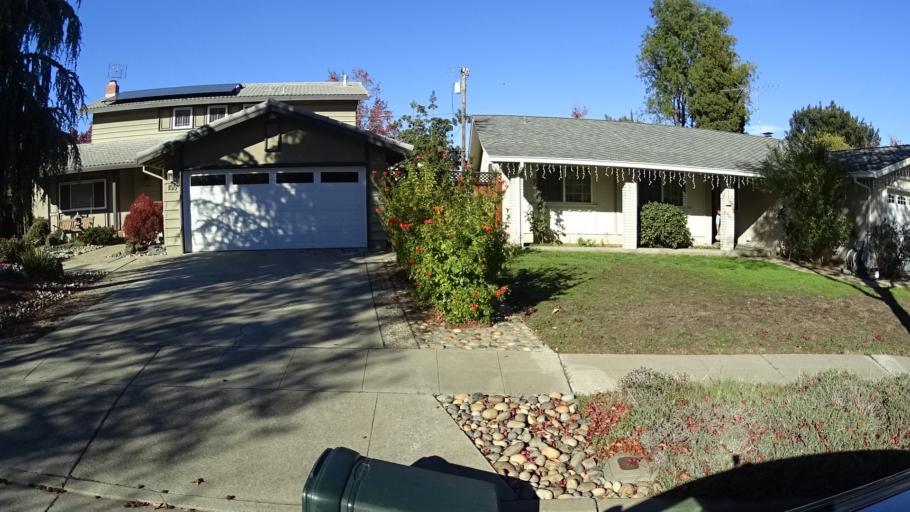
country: US
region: California
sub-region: Santa Clara County
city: Sunnyvale
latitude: 37.3471
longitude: -122.0303
